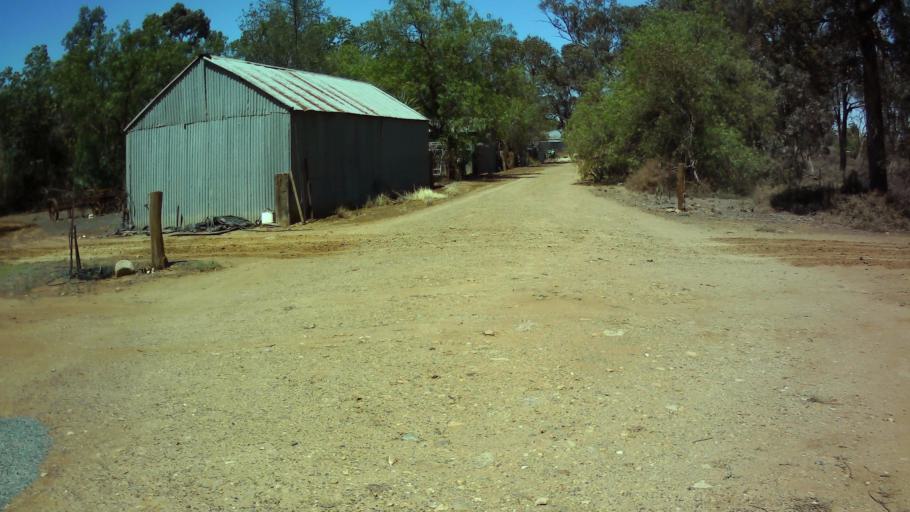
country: AU
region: New South Wales
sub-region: Weddin
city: Grenfell
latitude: -33.8442
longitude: 147.7370
